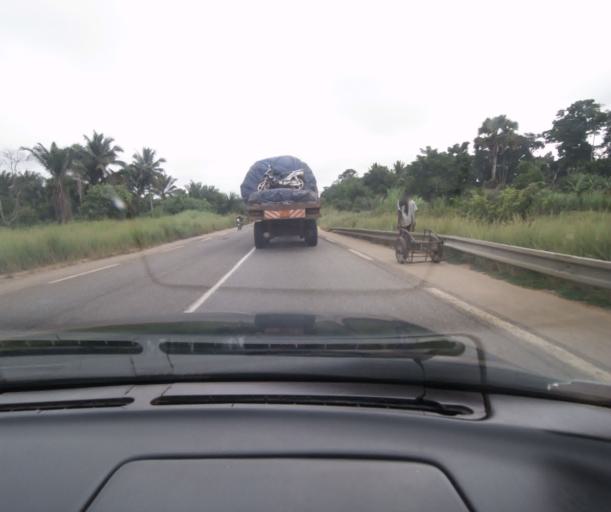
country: CM
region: Centre
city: Ombesa
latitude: 4.5760
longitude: 11.2666
